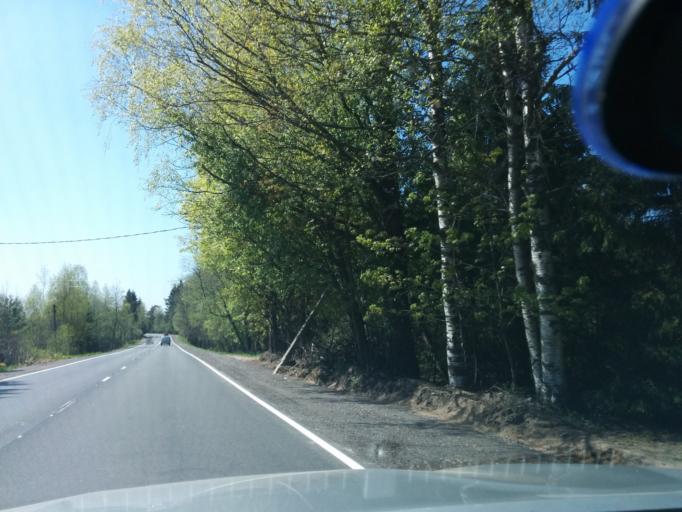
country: RU
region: Leningrad
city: Verkhniye Osel'ki
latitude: 60.2173
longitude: 30.4305
